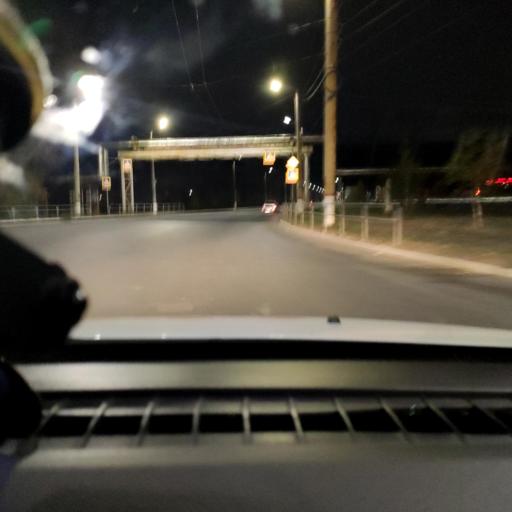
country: RU
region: Samara
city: Novokuybyshevsk
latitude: 53.1022
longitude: 49.9390
